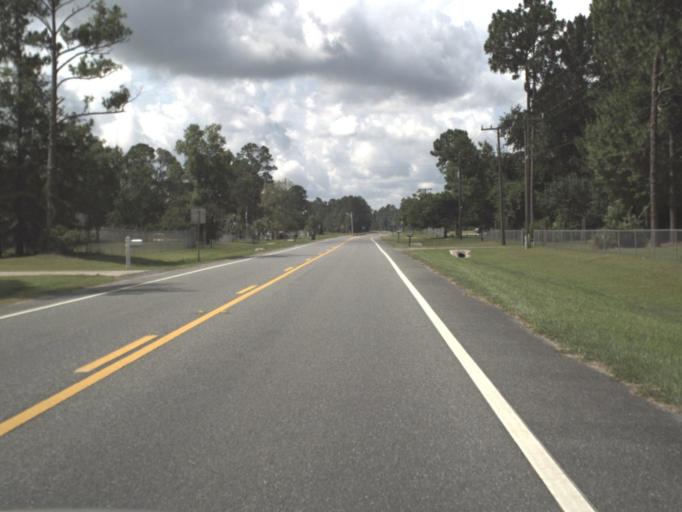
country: US
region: Florida
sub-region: Baker County
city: Macclenny
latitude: 30.3038
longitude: -82.1257
